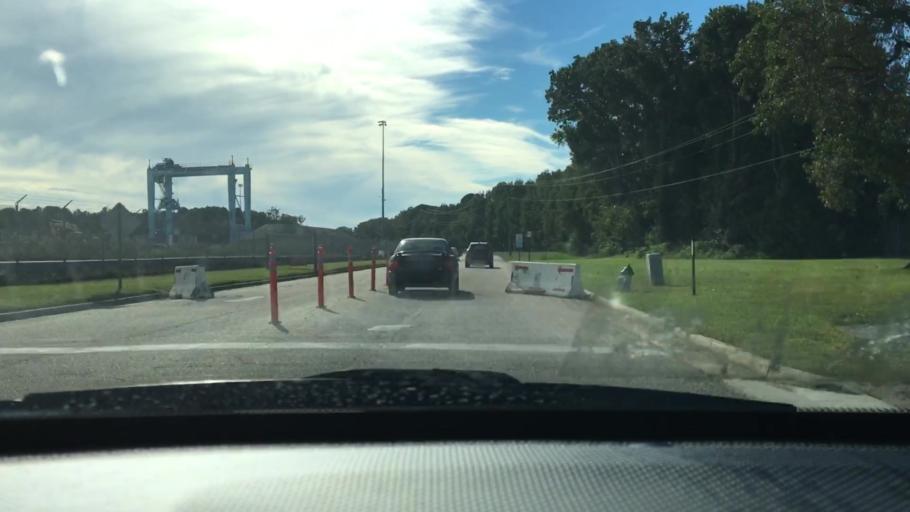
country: US
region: Virginia
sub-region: City of Portsmouth
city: Portsmouth Heights
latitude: 36.8803
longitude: -76.3610
